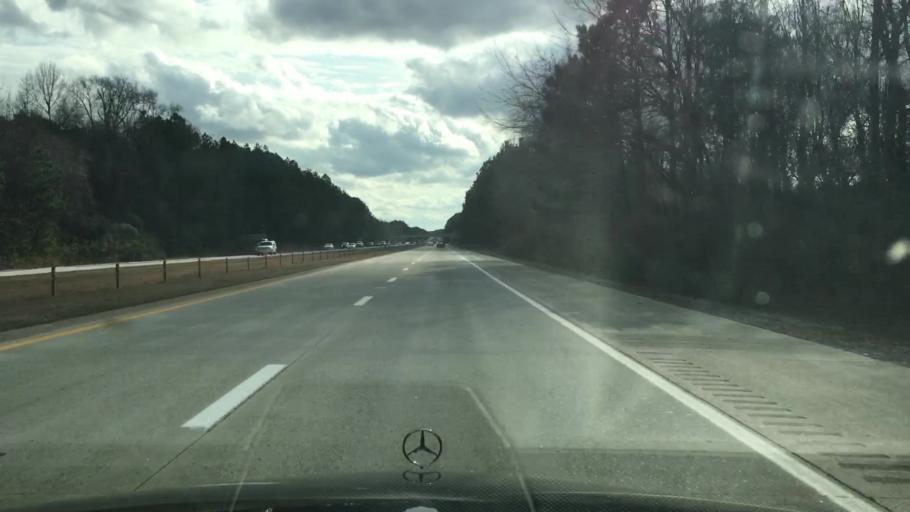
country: US
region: North Carolina
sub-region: Johnston County
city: Benson
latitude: 35.4962
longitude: -78.5535
